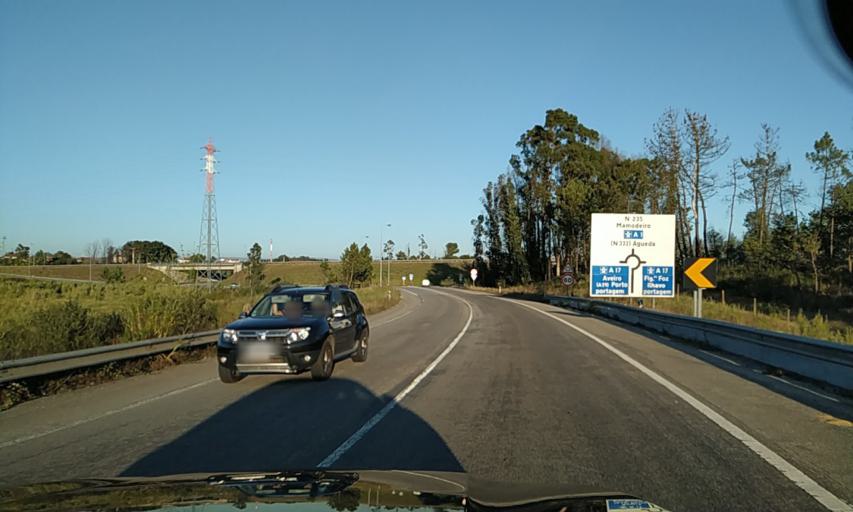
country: PT
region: Aveiro
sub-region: Aveiro
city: Oliveirinha
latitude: 40.5843
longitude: -8.6046
